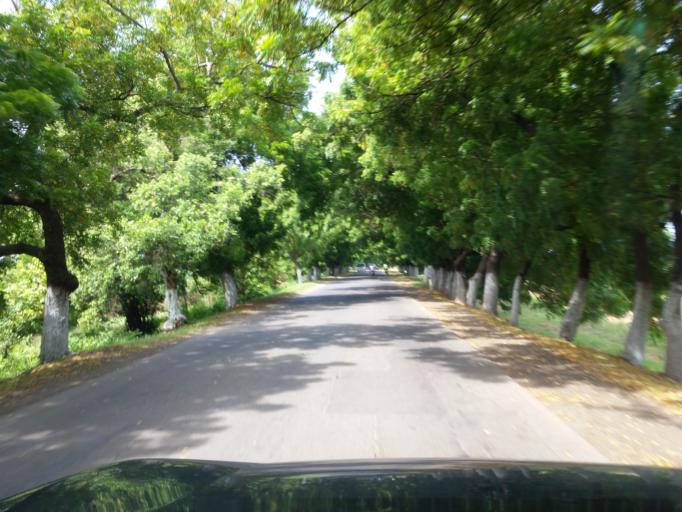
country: NI
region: Managua
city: Masachapa
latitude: 11.8030
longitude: -86.4976
